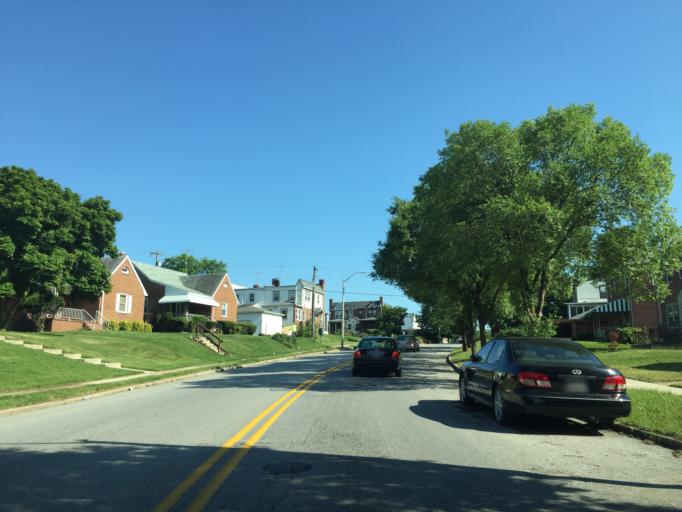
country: US
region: Maryland
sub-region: Baltimore County
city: Parkville
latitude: 39.3417
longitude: -76.5677
